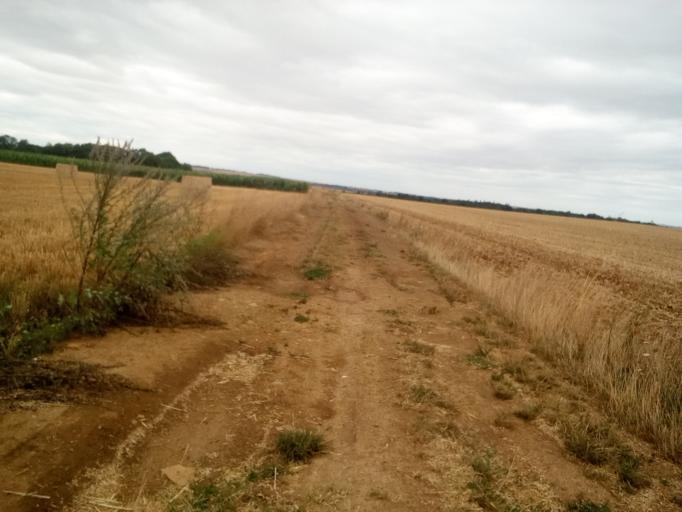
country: FR
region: Lower Normandy
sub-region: Departement du Calvados
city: Clinchamps-sur-Orne
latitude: 49.0608
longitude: -0.4131
